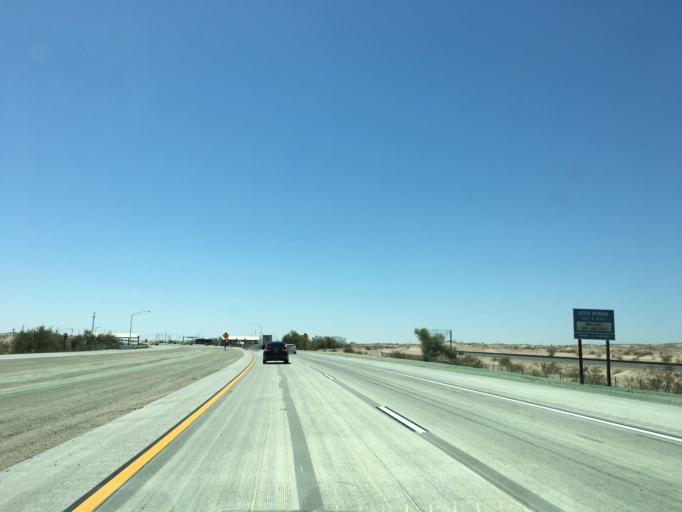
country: MX
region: Baja California
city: Los Algodones
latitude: 32.7465
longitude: -114.7368
